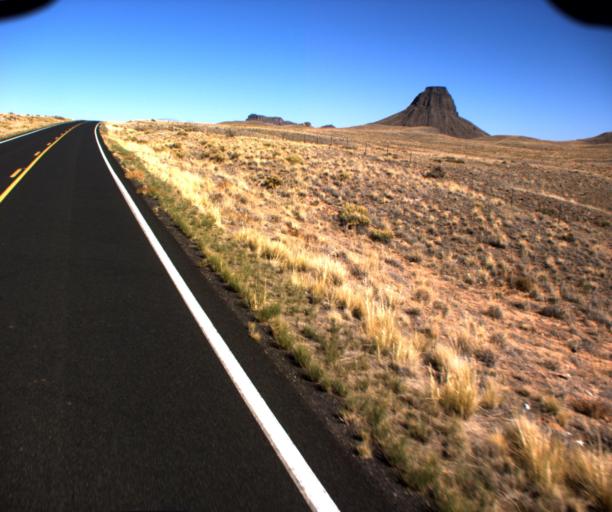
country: US
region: Arizona
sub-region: Navajo County
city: Dilkon
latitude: 35.2829
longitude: -110.4285
